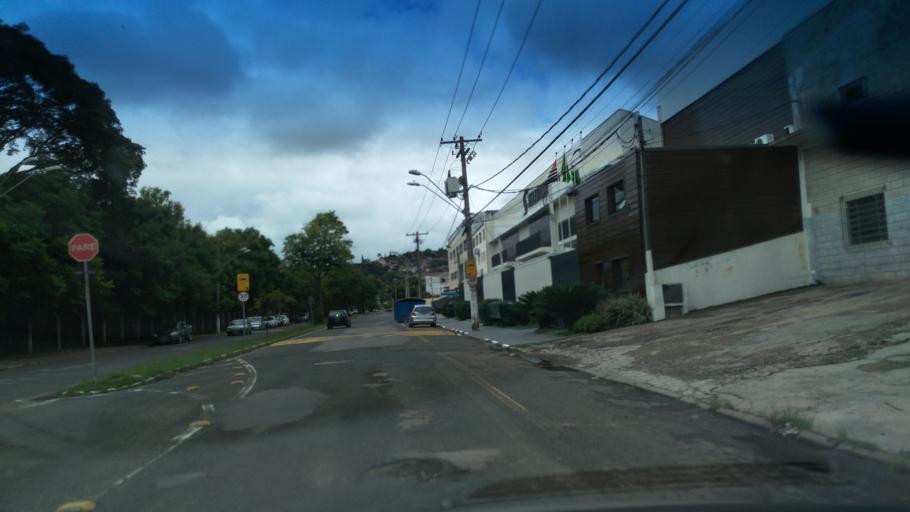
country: BR
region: Sao Paulo
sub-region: Valinhos
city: Valinhos
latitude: -22.9584
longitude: -46.9806
